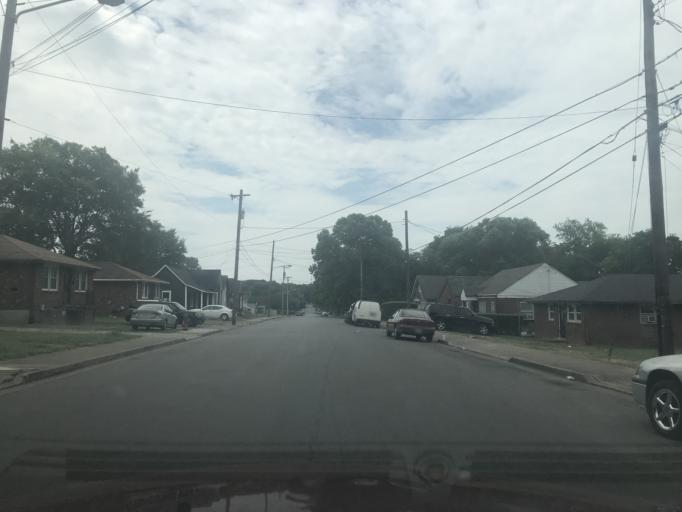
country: US
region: Tennessee
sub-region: Davidson County
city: Nashville
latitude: 36.1761
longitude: -86.8123
